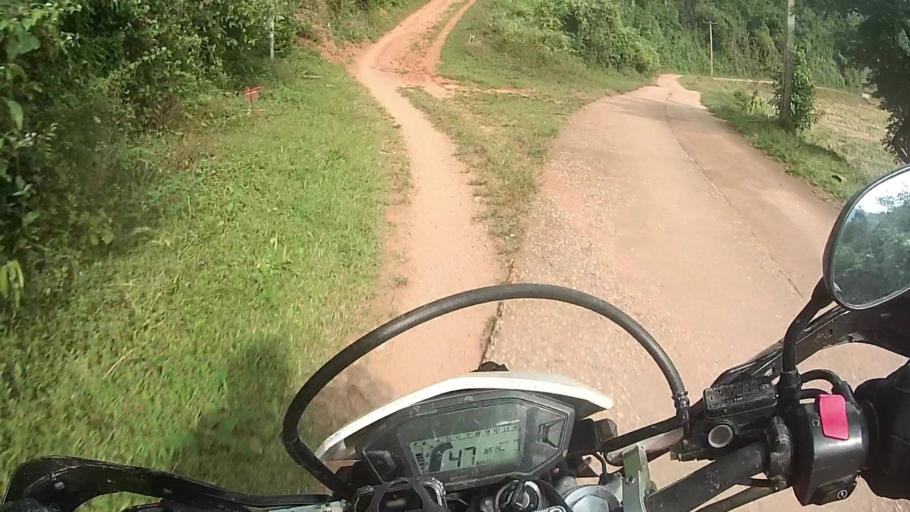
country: TH
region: Lampang
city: Wang Nuea
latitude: 19.0232
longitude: 99.4840
